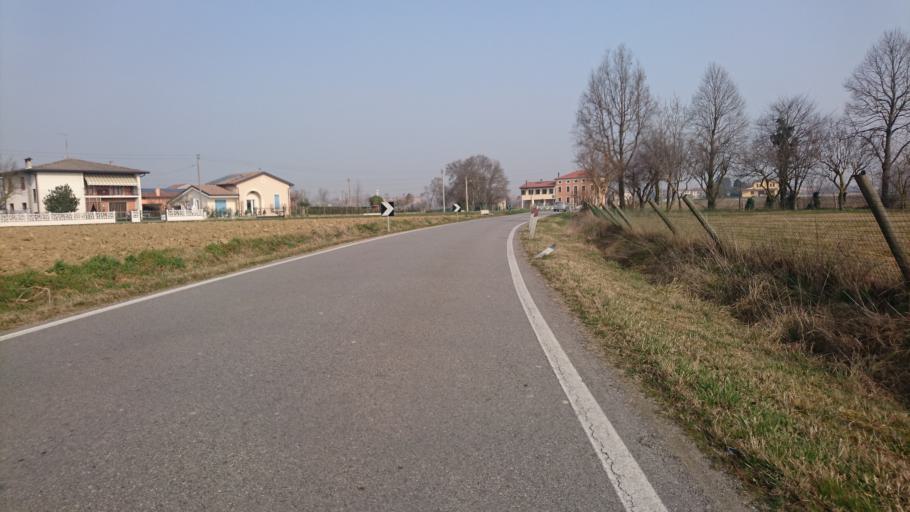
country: IT
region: Veneto
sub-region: Provincia di Padova
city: Veggiano
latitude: 45.4378
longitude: 11.7141
